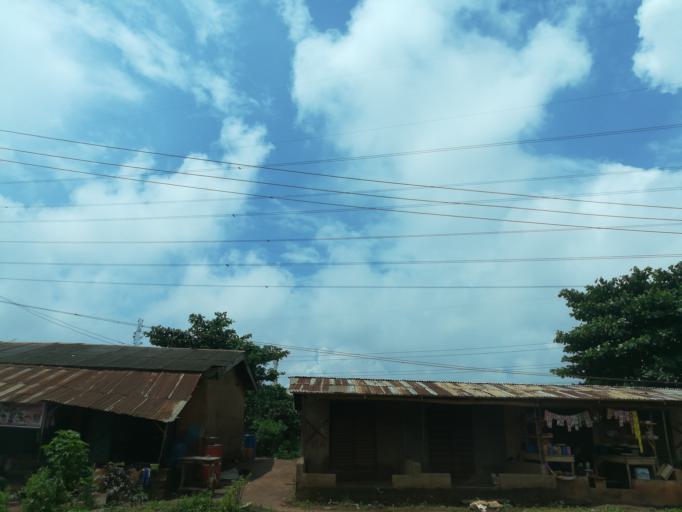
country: NG
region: Lagos
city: Ikorodu
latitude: 6.6801
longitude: 3.5126
